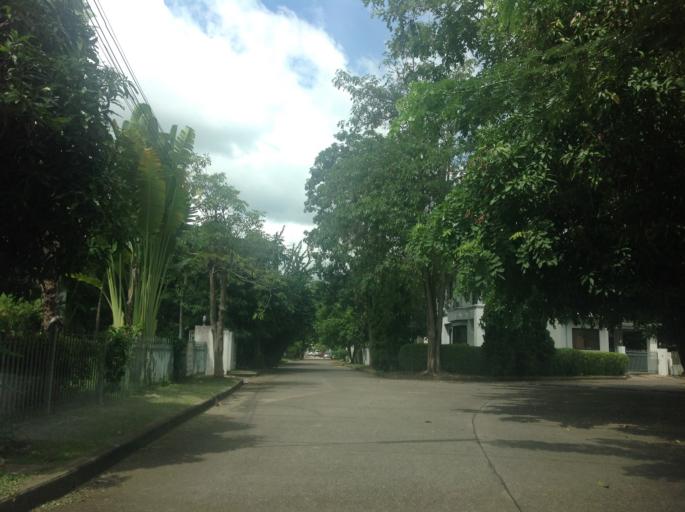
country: TH
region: Chiang Mai
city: Hang Dong
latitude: 18.7189
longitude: 98.9260
